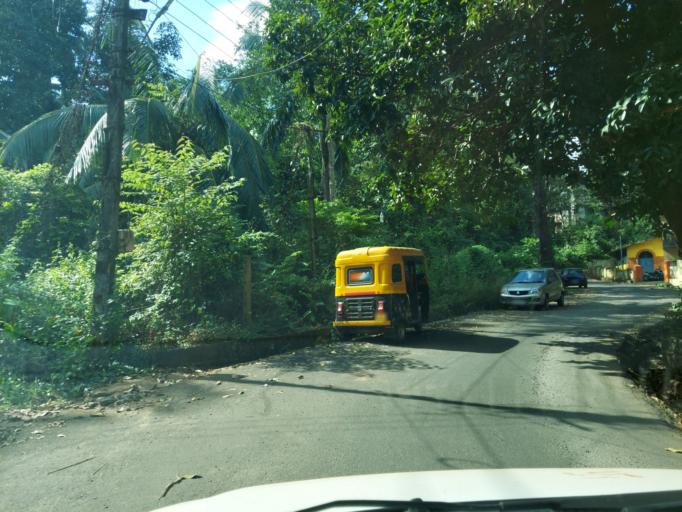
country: IN
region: Maharashtra
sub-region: Sindhudurg
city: Savantvadi
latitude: 15.9048
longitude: 73.8159
